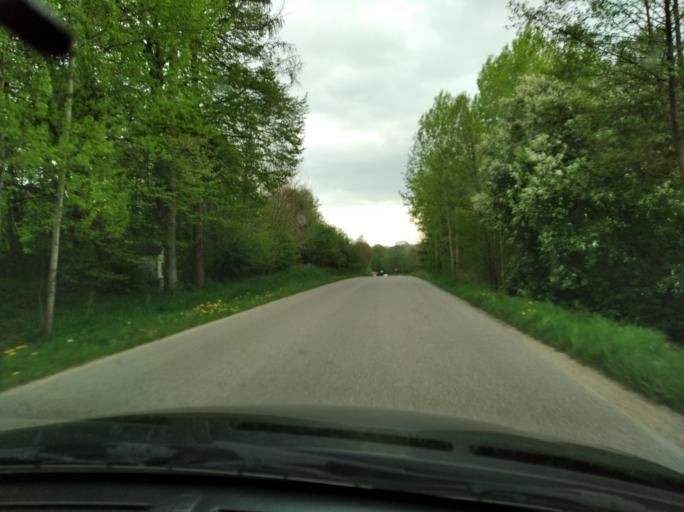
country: PL
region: Subcarpathian Voivodeship
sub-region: Powiat debicki
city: Leki Gorne
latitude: 49.9803
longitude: 21.1573
